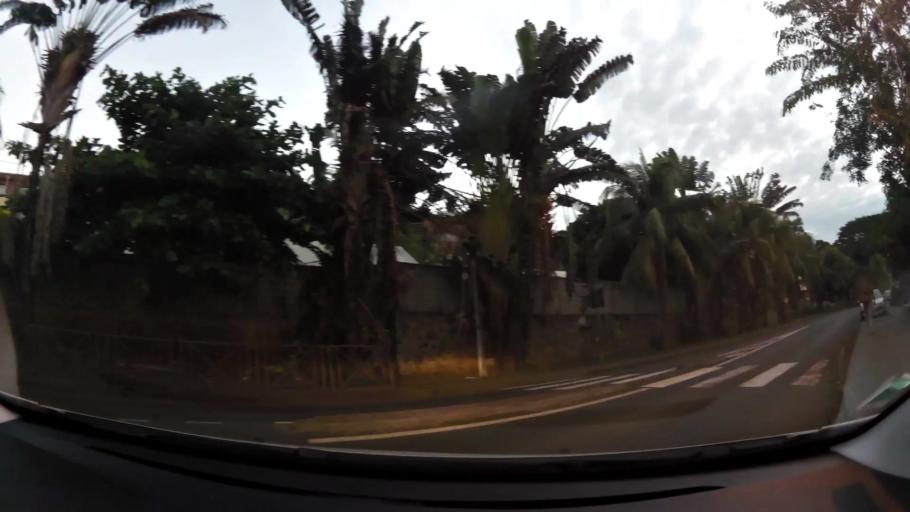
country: YT
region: Bandraboua
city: Bandraboua
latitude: -12.7352
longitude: 45.1394
